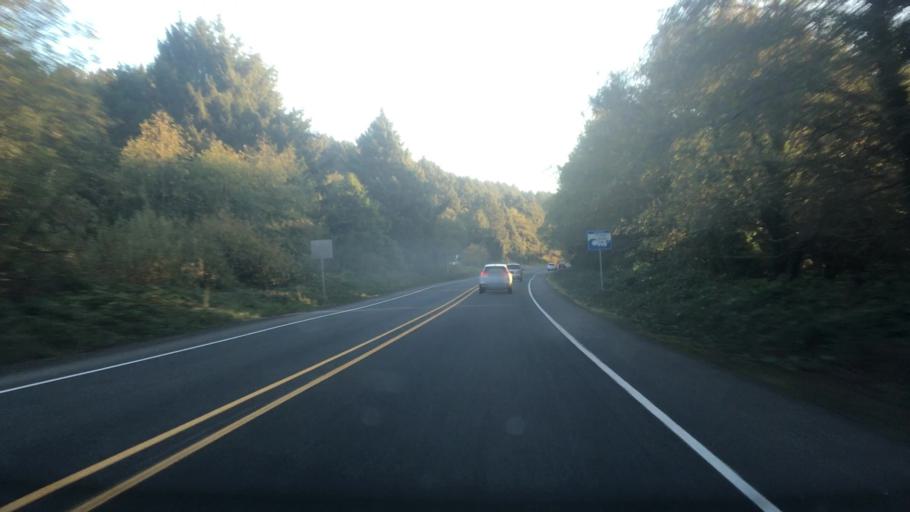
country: US
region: Oregon
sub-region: Clatsop County
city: Cannon Beach
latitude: 45.8654
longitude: -123.9589
